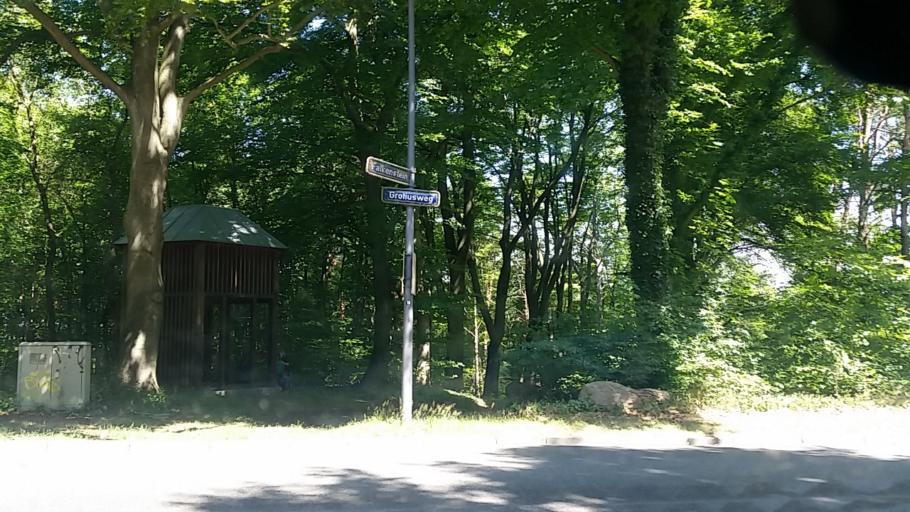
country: DE
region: Schleswig-Holstein
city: Wedel
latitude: 53.5687
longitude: 9.7728
